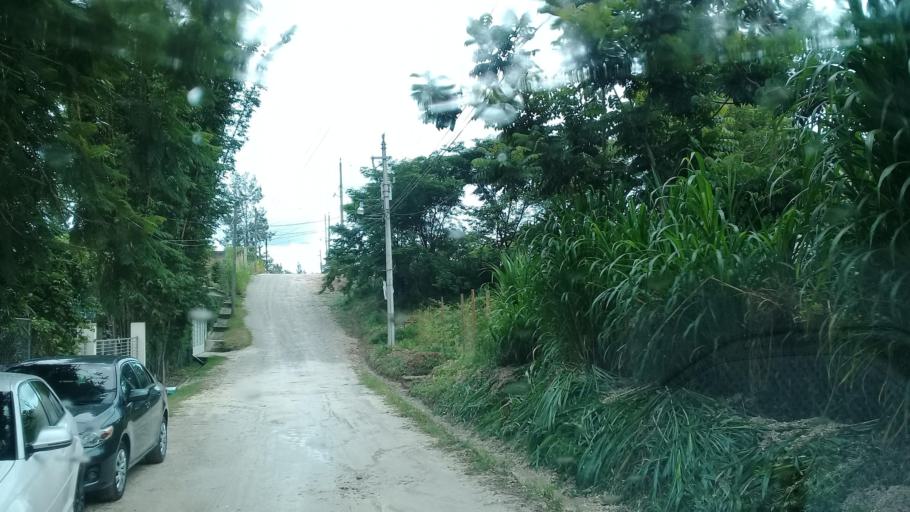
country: MX
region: Veracruz
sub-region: Emiliano Zapata
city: Jacarandas
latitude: 19.5053
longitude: -96.8410
